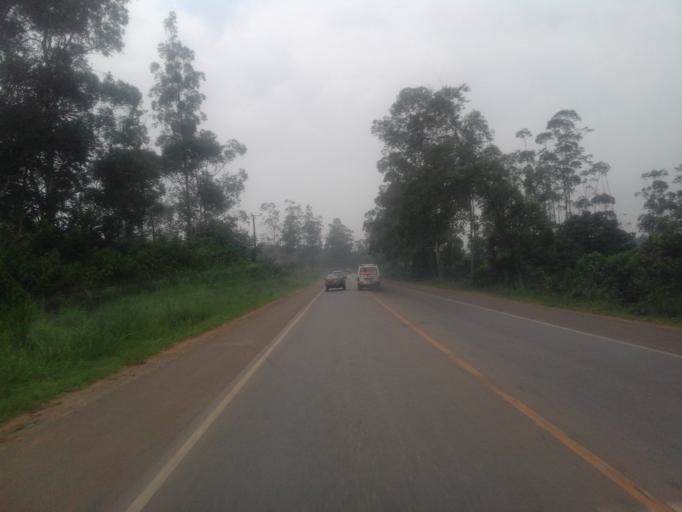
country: UG
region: Central Region
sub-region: Mukono District
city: Mukono
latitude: 0.3583
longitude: 32.7975
